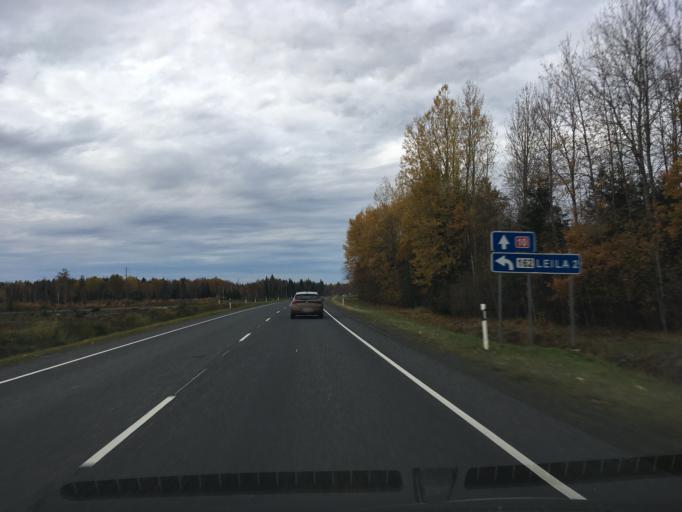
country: EE
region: Harju
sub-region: Nissi vald
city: Turba
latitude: 58.9392
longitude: 24.0905
